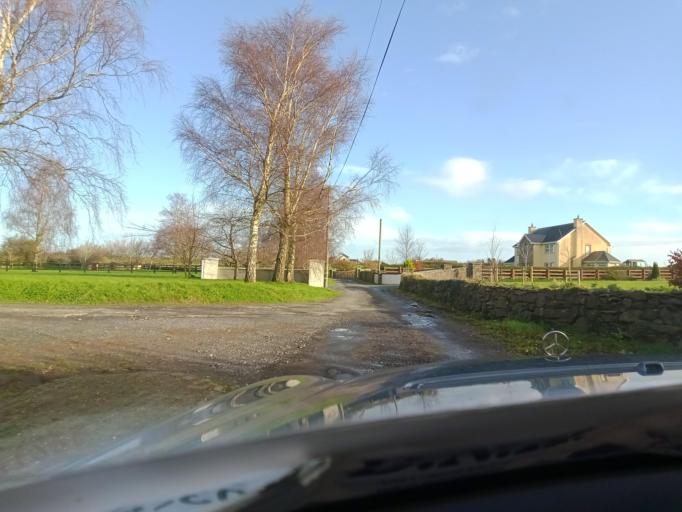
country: IE
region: Leinster
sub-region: Kilkenny
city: Mooncoin
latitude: 52.2775
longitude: -7.2569
